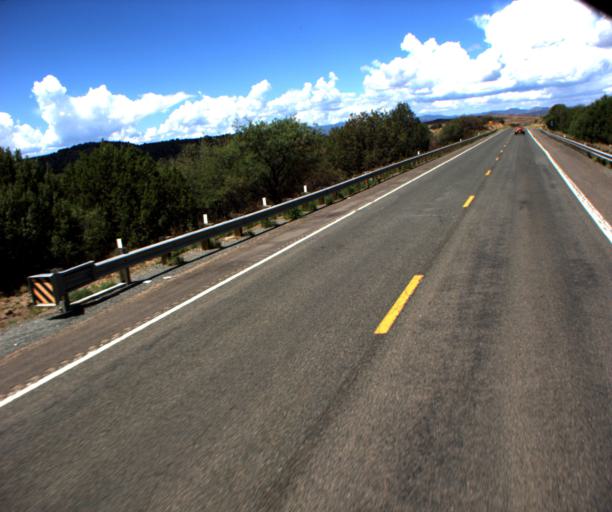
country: US
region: Arizona
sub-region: Yavapai County
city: Camp Verde
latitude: 34.5146
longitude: -112.0102
